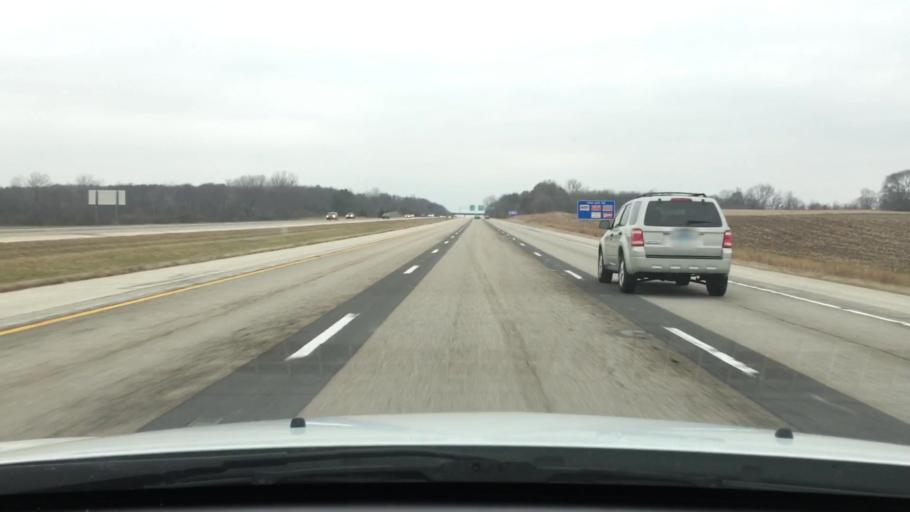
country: US
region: Illinois
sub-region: Logan County
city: Lincoln
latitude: 40.1363
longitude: -89.4169
